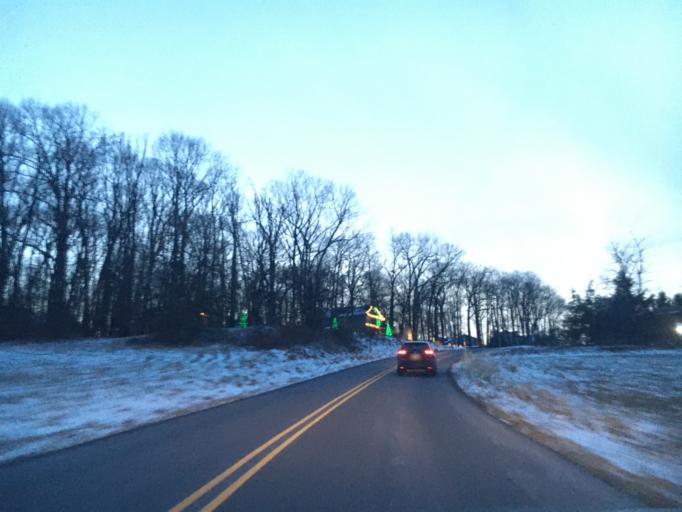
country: US
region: Pennsylvania
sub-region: Northampton County
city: Cherryville
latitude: 40.7460
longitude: -75.5272
